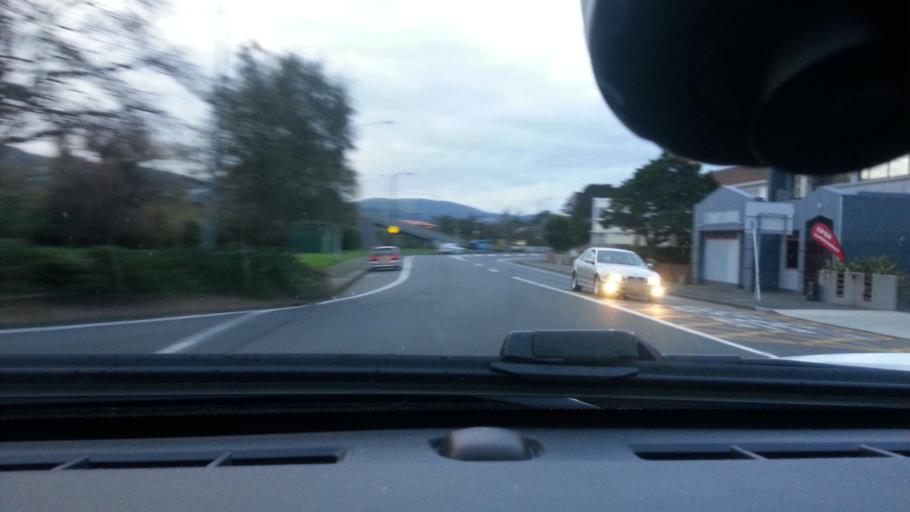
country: NZ
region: Wellington
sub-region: Lower Hutt City
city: Lower Hutt
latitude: -41.2228
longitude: 174.9106
